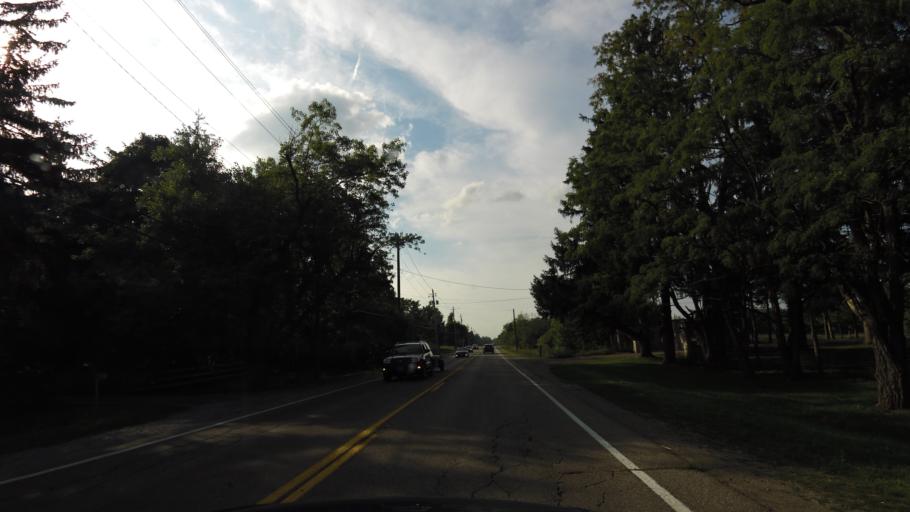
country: CA
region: Ontario
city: Burlington
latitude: 43.3714
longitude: -79.8664
